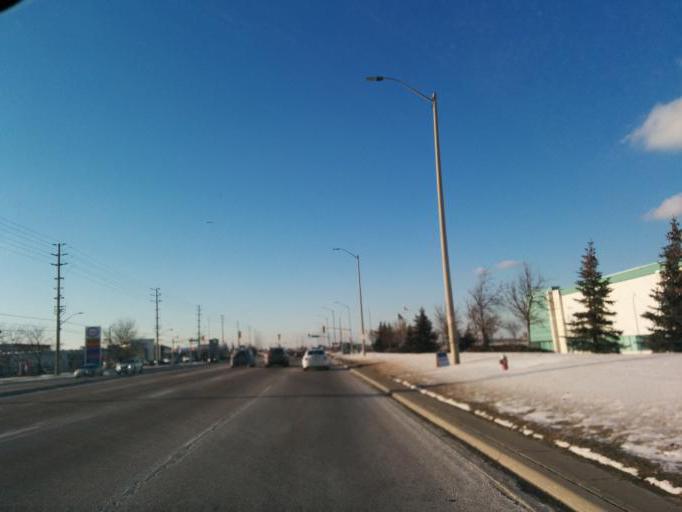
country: CA
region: Ontario
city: Mississauga
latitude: 43.6161
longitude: -79.7010
